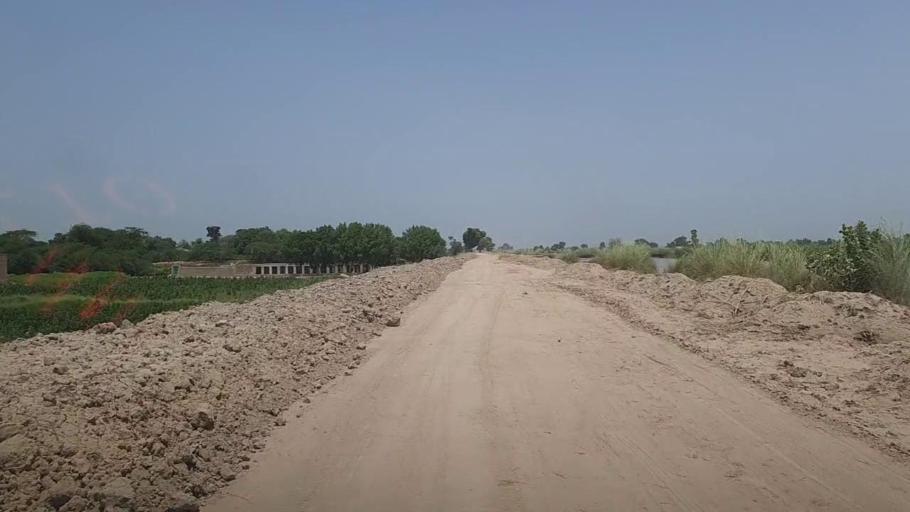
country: PK
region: Sindh
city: Pad Idan
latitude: 26.7895
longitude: 68.2764
